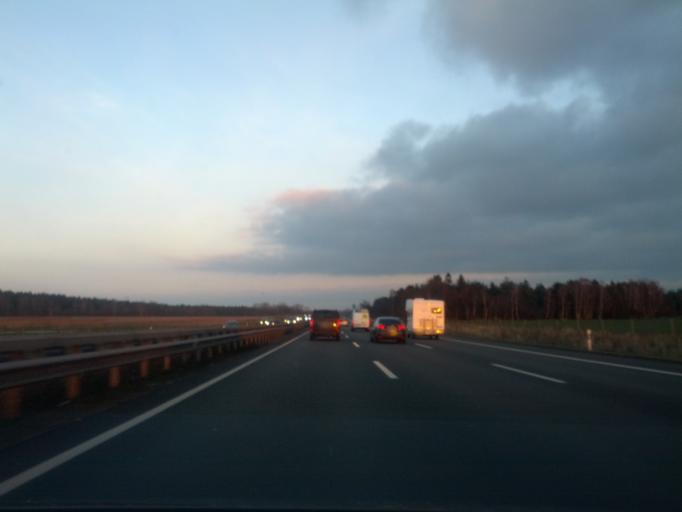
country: DE
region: Lower Saxony
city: Kalbe
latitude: 53.3107
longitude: 9.5593
